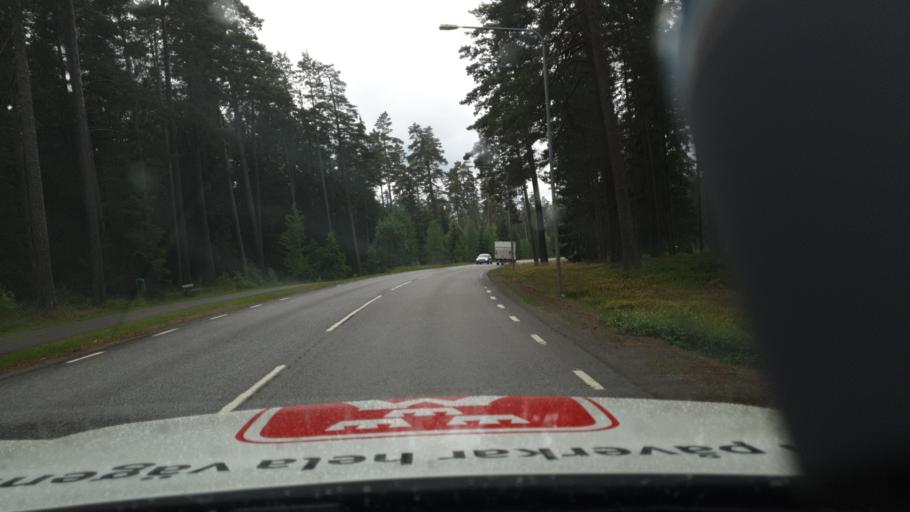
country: SE
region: Joenkoeping
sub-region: Mullsjo Kommun
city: Mullsjoe
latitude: 57.9108
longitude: 13.8734
